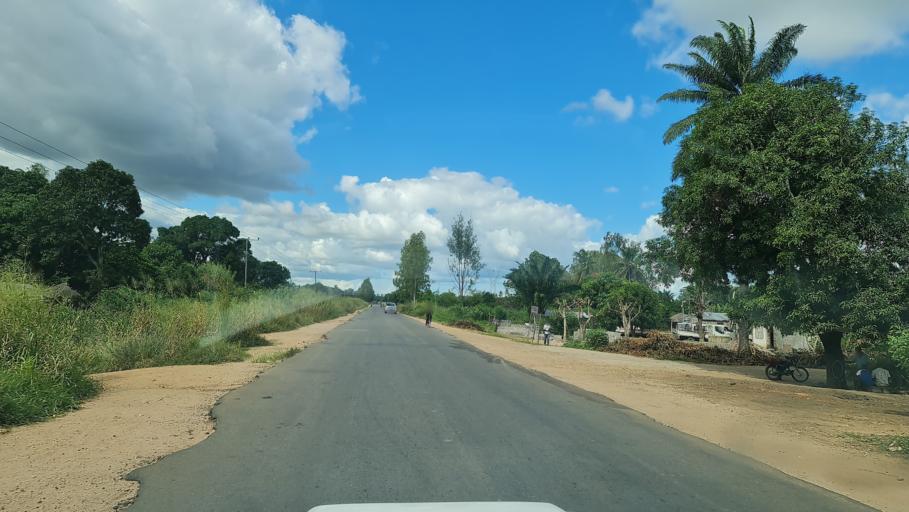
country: MZ
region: Zambezia
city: Quelimane
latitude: -17.5979
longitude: 36.7909
